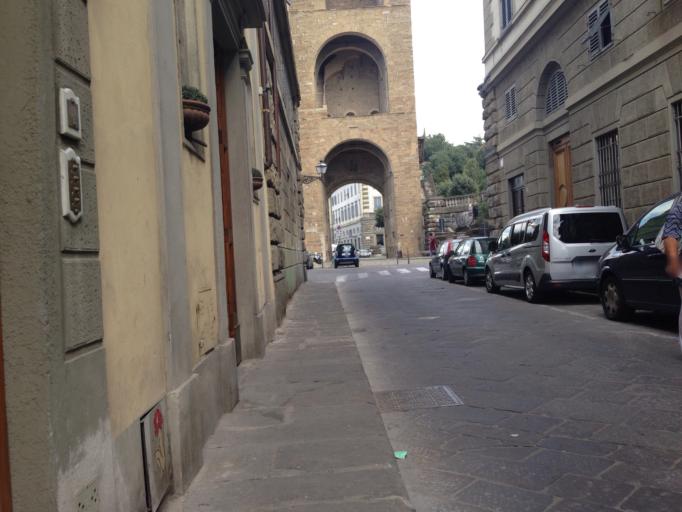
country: IT
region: Tuscany
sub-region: Province of Florence
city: Florence
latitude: 43.7644
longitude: 11.2639
